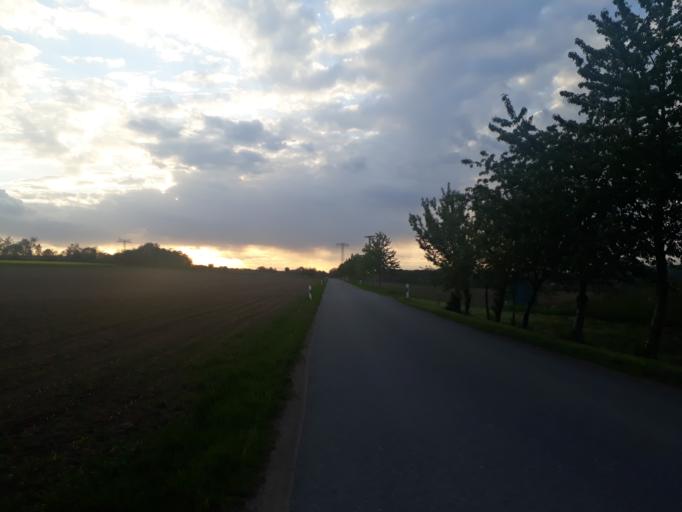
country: DE
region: Saxony
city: Reinhardtsgrimma
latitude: 50.8955
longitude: 13.7542
